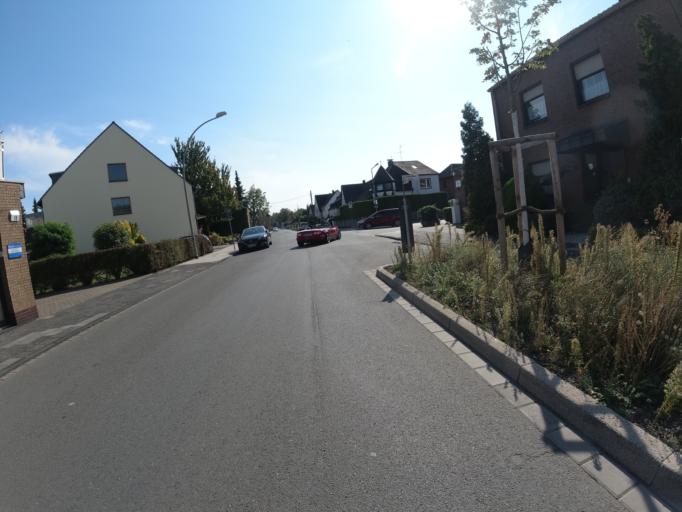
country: DE
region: North Rhine-Westphalia
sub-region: Regierungsbezirk Dusseldorf
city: Moers
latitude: 51.4616
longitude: 6.6924
